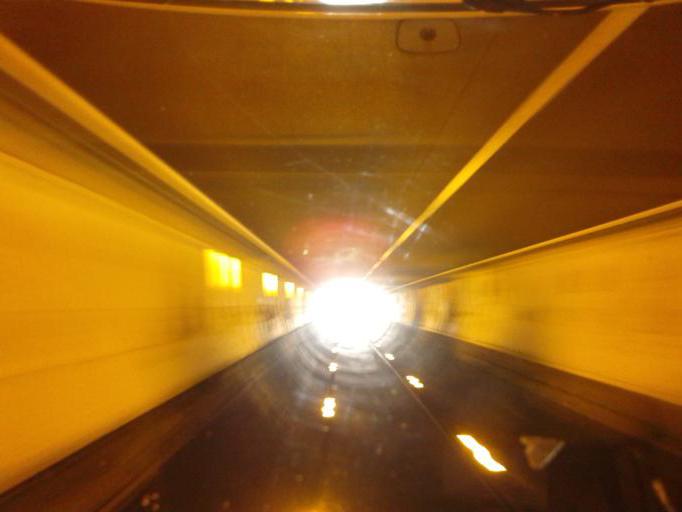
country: IT
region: Liguria
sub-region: Provincia di Imperia
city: Vallebona
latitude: 43.8012
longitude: 7.6553
